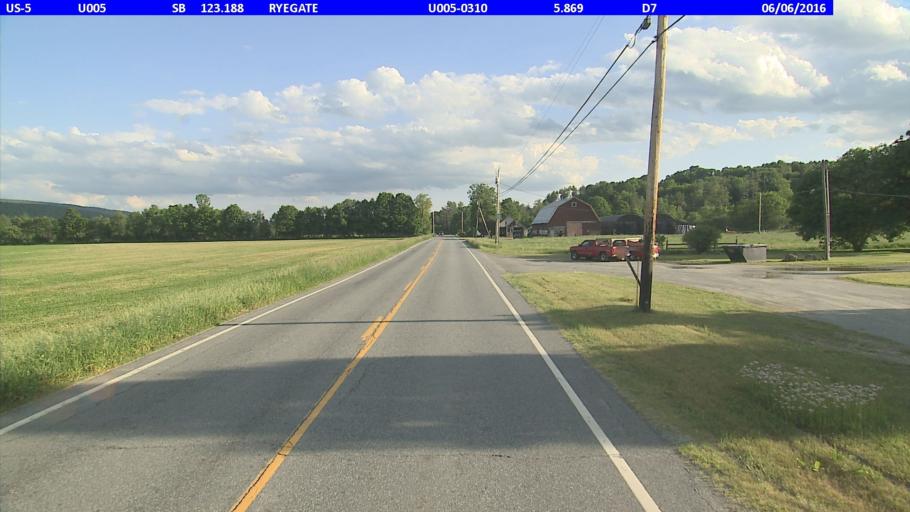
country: US
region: New Hampshire
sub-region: Grafton County
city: Woodsville
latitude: 44.2360
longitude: -72.0561
